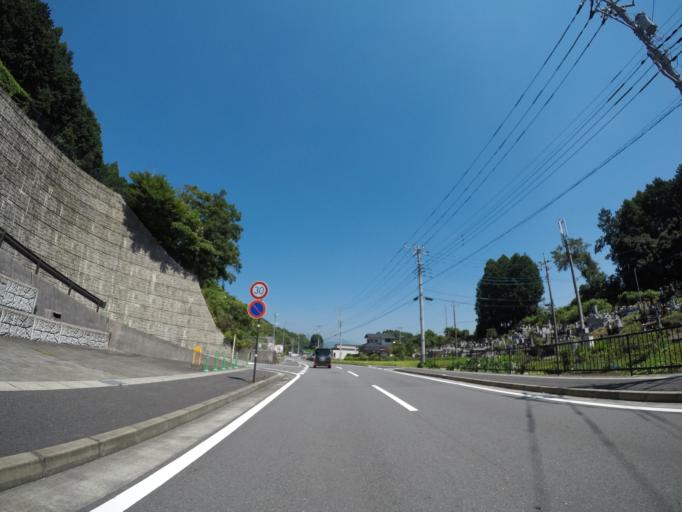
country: JP
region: Shizuoka
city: Fujinomiya
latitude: 35.2071
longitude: 138.5656
